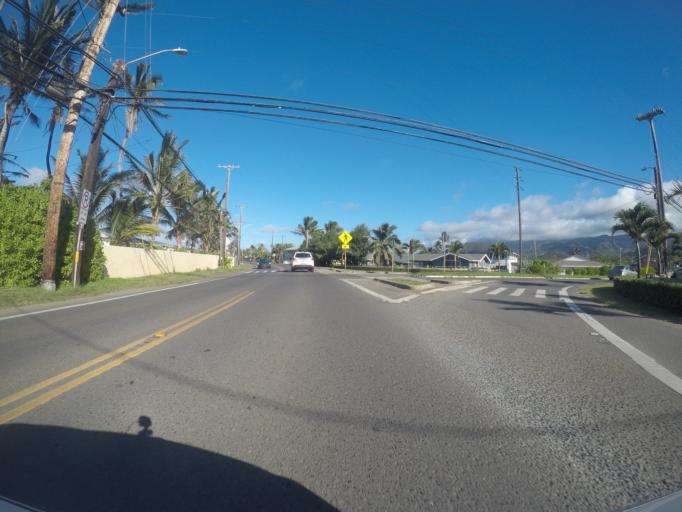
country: US
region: Hawaii
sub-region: Honolulu County
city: La'ie
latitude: 21.6523
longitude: -157.9287
